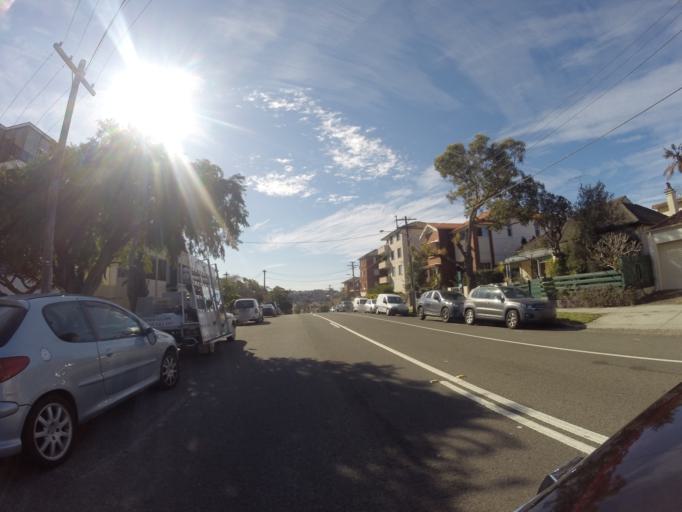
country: AU
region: New South Wales
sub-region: Randwick
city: Coogee
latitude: -33.9238
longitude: 151.2512
